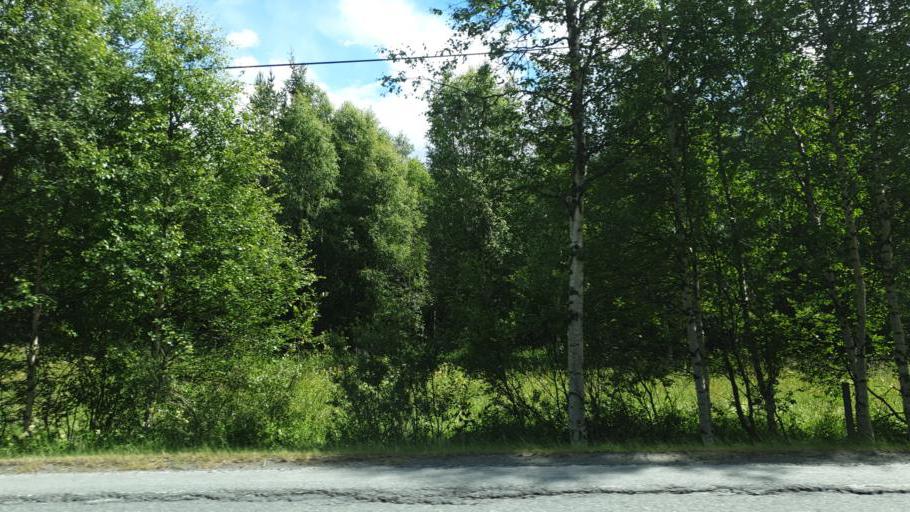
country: NO
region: Sor-Trondelag
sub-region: Rennebu
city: Berkak
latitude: 62.7092
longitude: 9.9553
